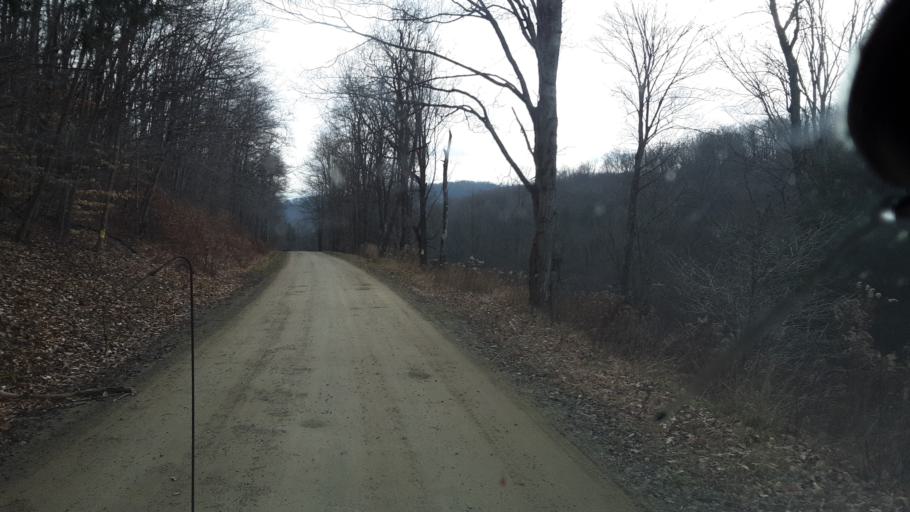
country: US
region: Pennsylvania
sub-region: Tioga County
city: Westfield
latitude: 41.9081
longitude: -77.7179
